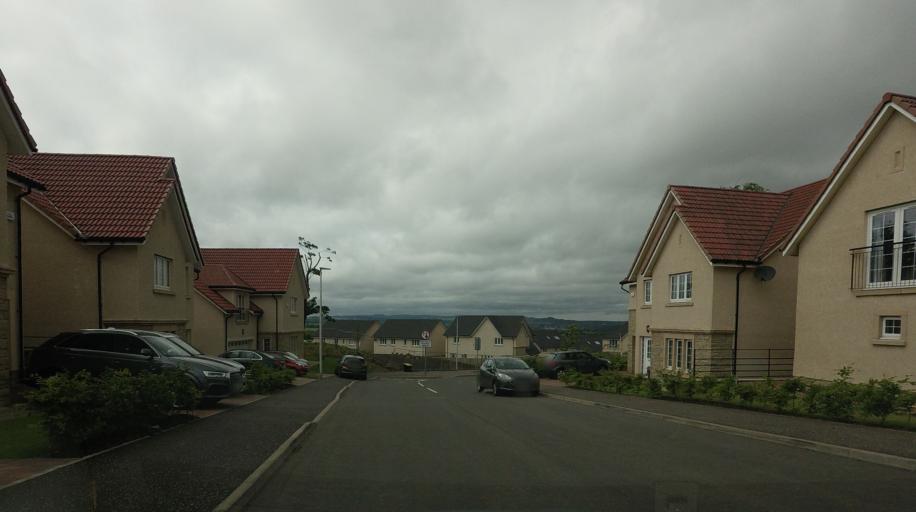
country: GB
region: Scotland
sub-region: Edinburgh
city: Ratho
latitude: 55.9203
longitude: -3.3930
